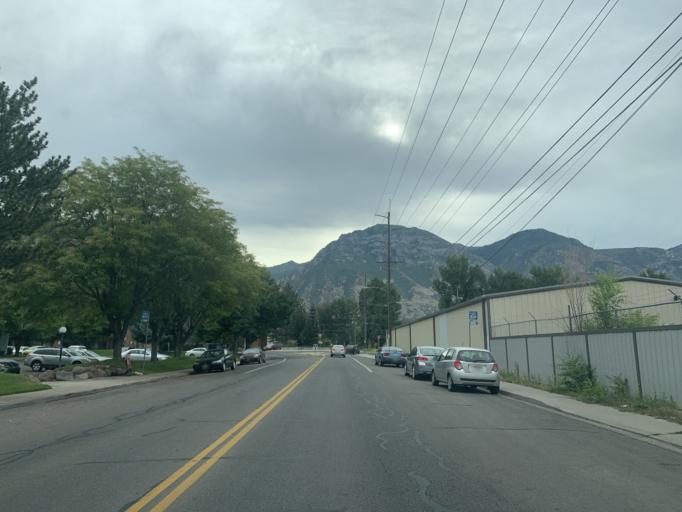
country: US
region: Utah
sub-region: Utah County
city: Provo
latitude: 40.2569
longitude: -111.6693
